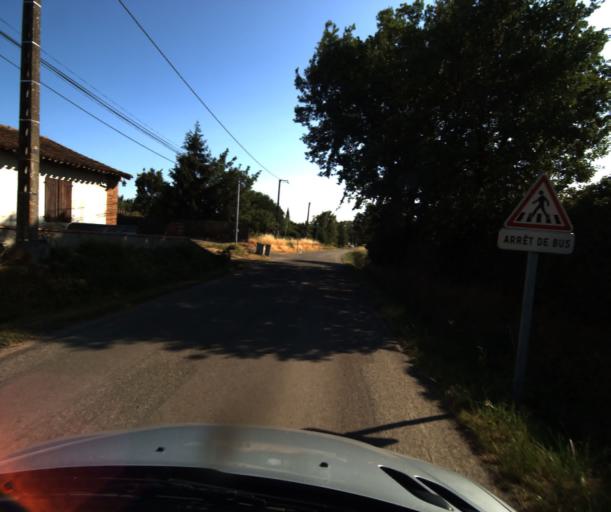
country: FR
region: Midi-Pyrenees
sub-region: Departement du Tarn-et-Garonne
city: Bressols
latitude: 43.9612
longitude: 1.3077
